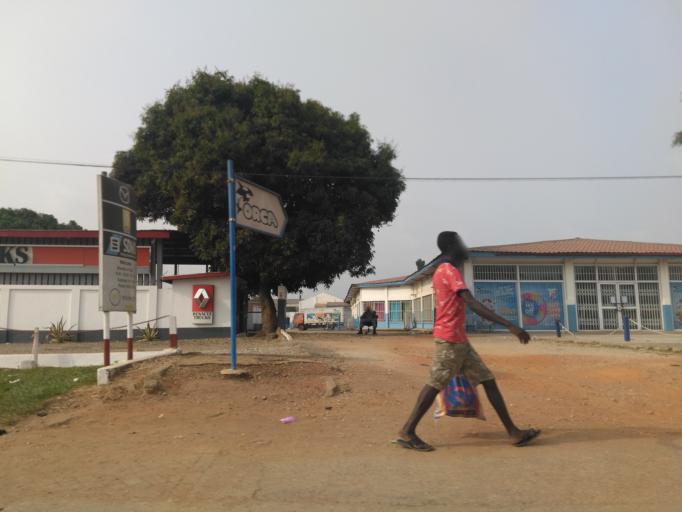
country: GH
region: Ashanti
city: Kumasi
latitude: 6.6654
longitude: -1.6039
